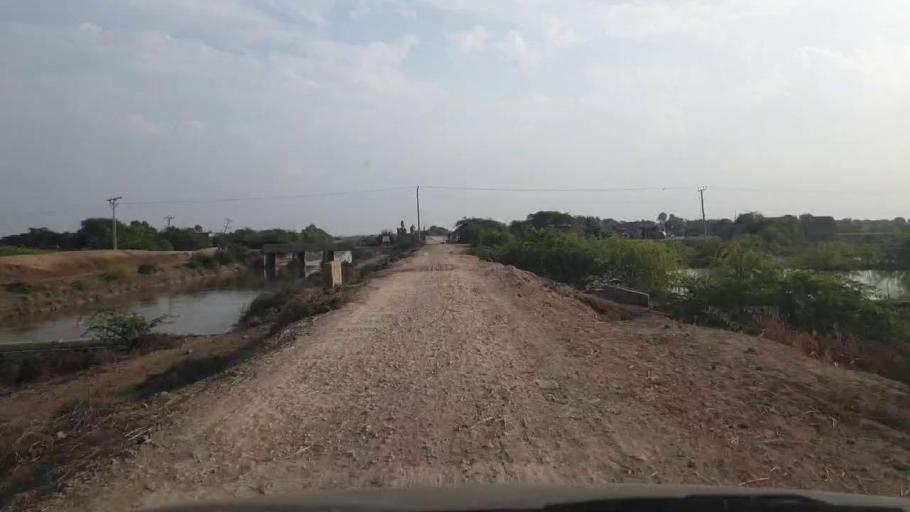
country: PK
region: Sindh
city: Badin
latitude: 24.5505
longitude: 68.6708
